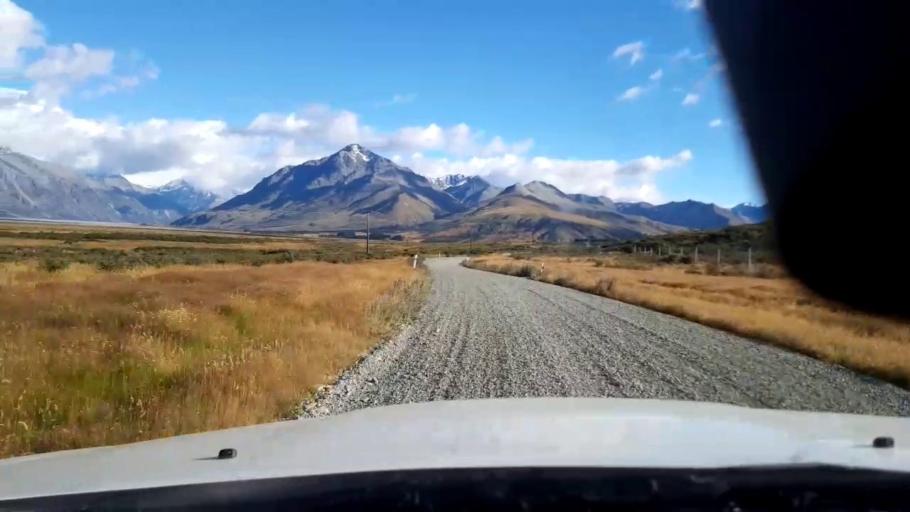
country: NZ
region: Canterbury
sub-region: Timaru District
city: Pleasant Point
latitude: -43.7485
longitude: 170.5715
